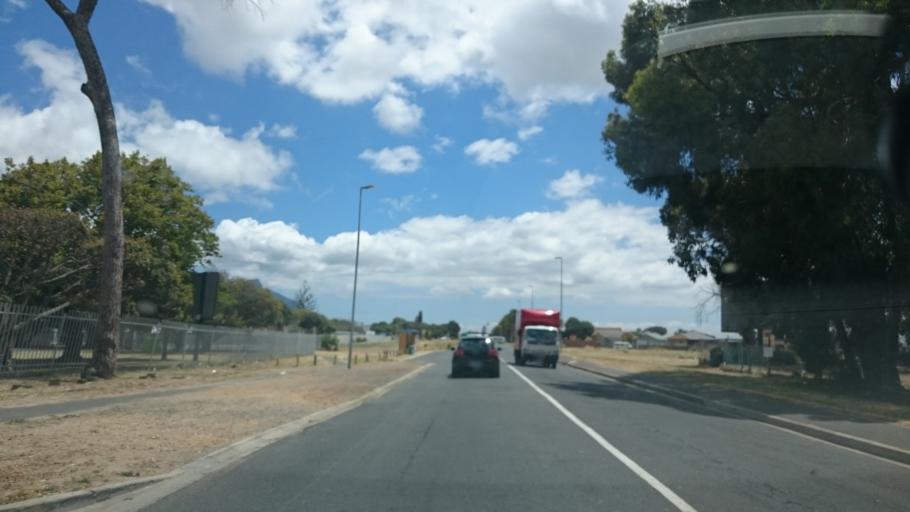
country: ZA
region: Western Cape
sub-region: City of Cape Town
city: Bergvliet
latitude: -34.0588
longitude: 18.4603
